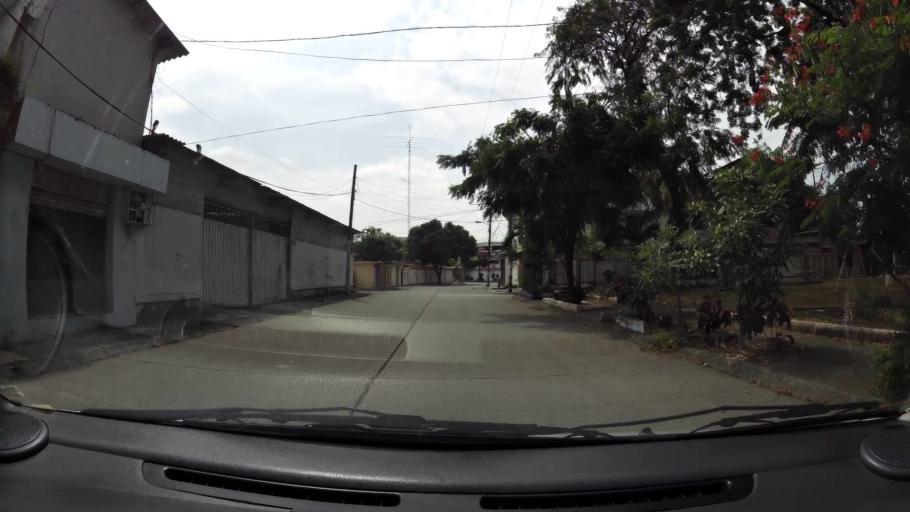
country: EC
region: Guayas
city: Eloy Alfaro
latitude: -2.1223
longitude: -79.8960
